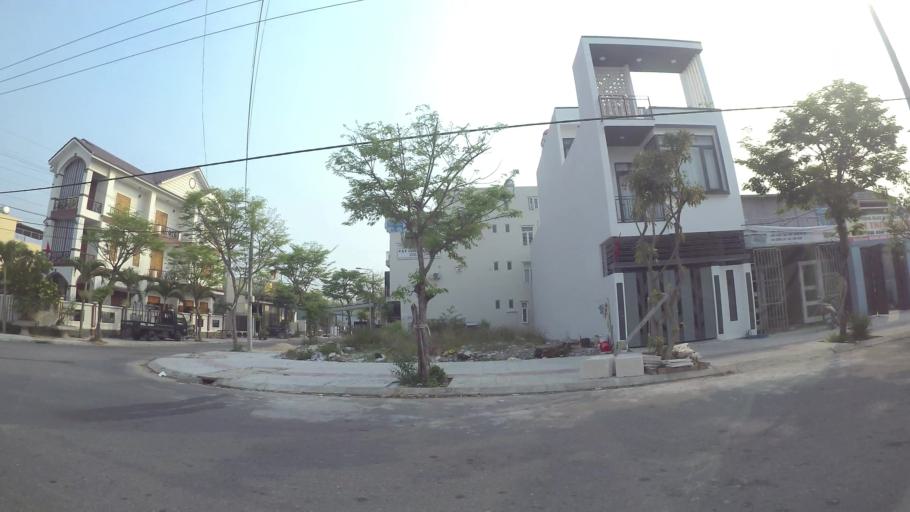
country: VN
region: Da Nang
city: Cam Le
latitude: 16.0086
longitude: 108.2218
